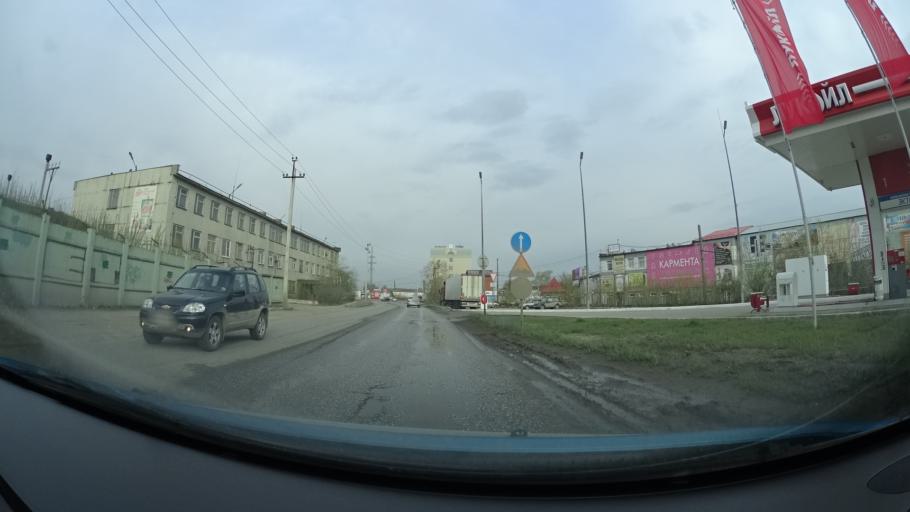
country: RU
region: Perm
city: Kondratovo
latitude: 58.0033
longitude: 56.1576
